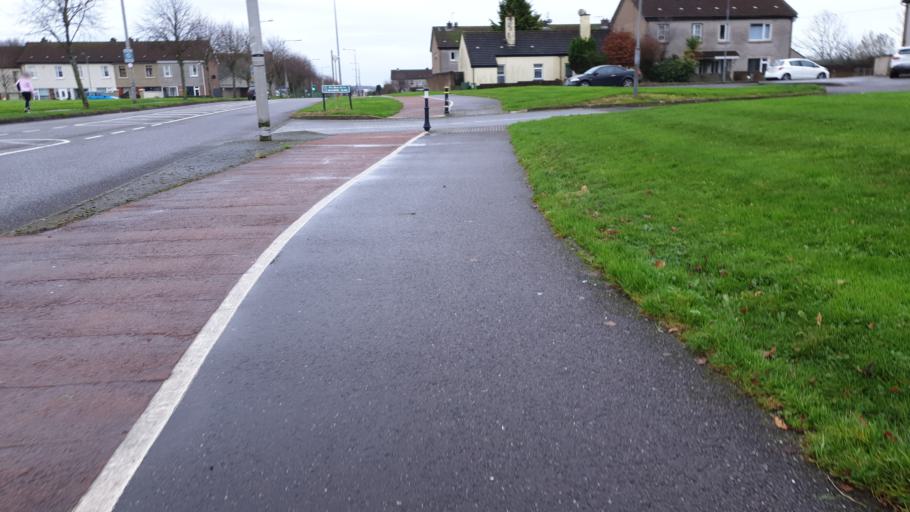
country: IE
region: Munster
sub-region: County Cork
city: Cork
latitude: 51.8906
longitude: -8.4073
